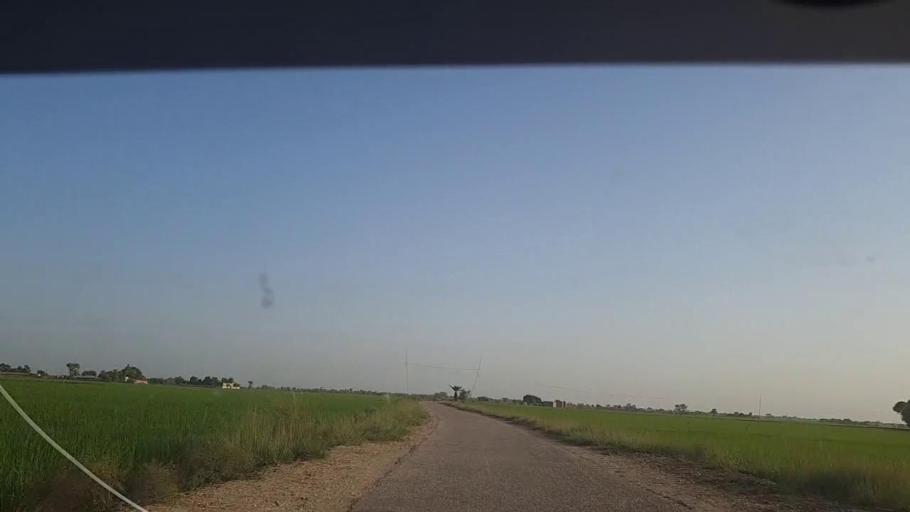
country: PK
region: Sindh
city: Thul
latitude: 28.2001
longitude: 68.8741
